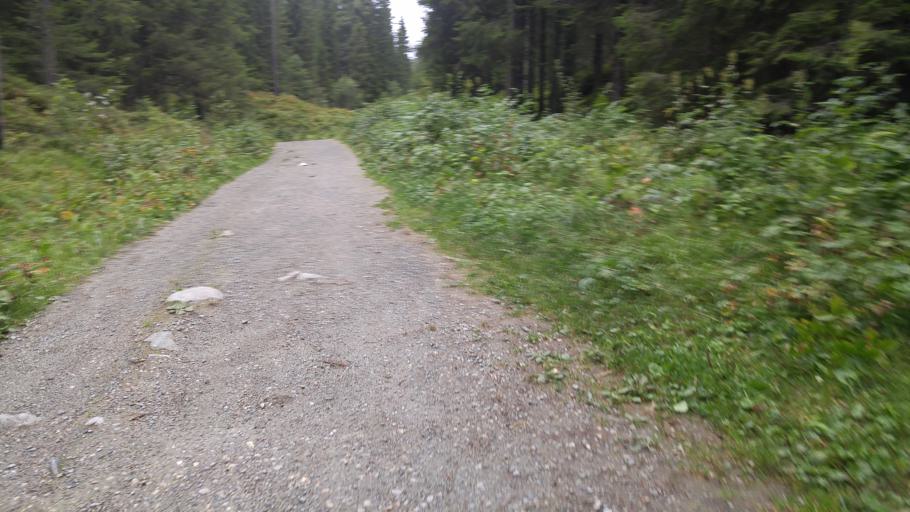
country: NO
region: Sor-Trondelag
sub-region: Trondheim
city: Trondheim
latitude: 63.4104
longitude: 10.3321
